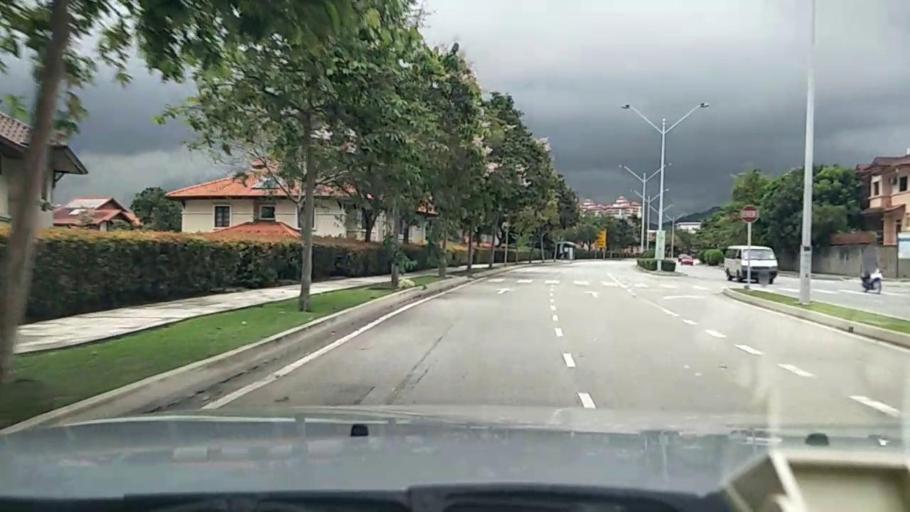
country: MY
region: Putrajaya
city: Putrajaya
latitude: 2.9323
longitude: 101.7025
